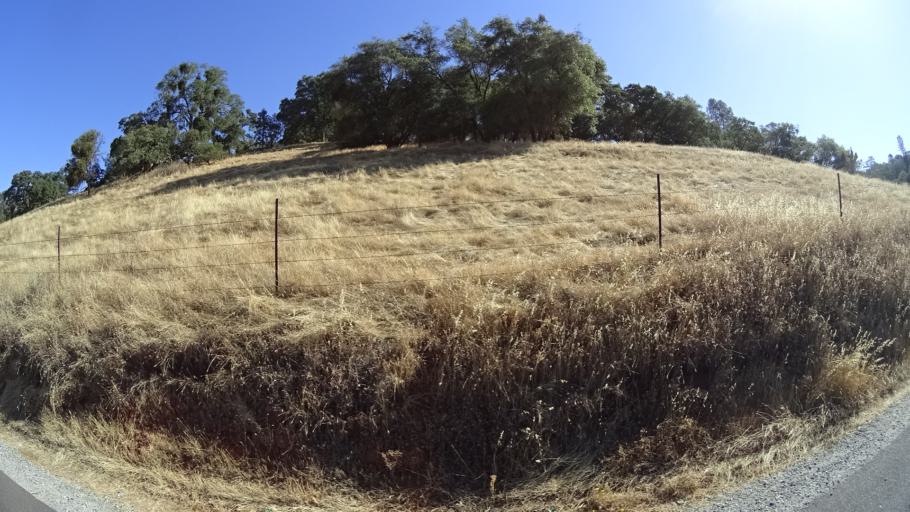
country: US
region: California
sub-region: Calaveras County
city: San Andreas
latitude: 38.2273
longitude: -120.6742
